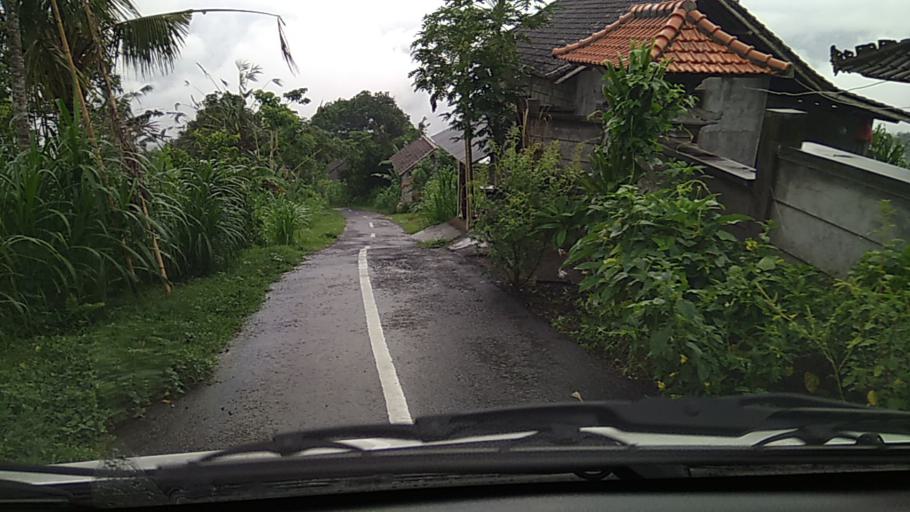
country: ID
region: Bali
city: Tiyingtali Kelod
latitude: -8.3968
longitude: 115.6349
